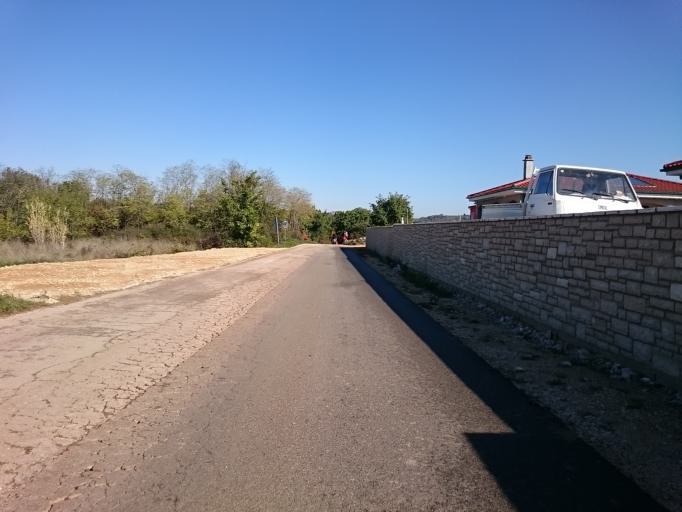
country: HR
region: Istarska
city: Buje
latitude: 45.4242
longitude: 13.6767
